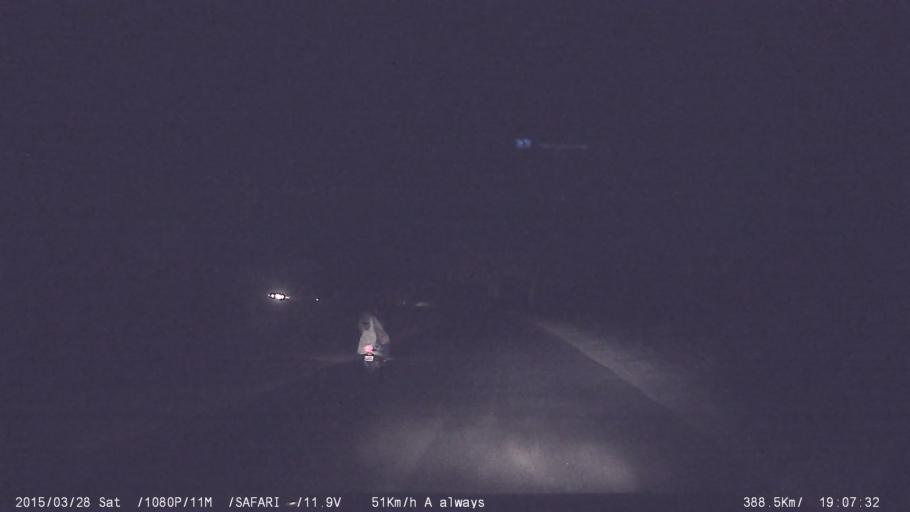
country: IN
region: Karnataka
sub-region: Mandya
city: Shrirangapattana
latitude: 12.3921
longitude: 76.6154
